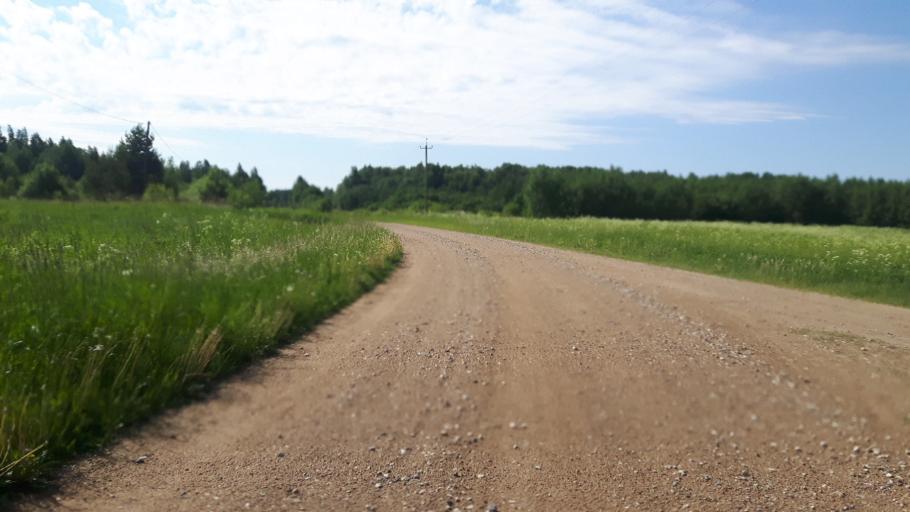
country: EE
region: Paernumaa
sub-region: Vaendra vald (alev)
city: Vandra
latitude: 58.7032
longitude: 25.0283
